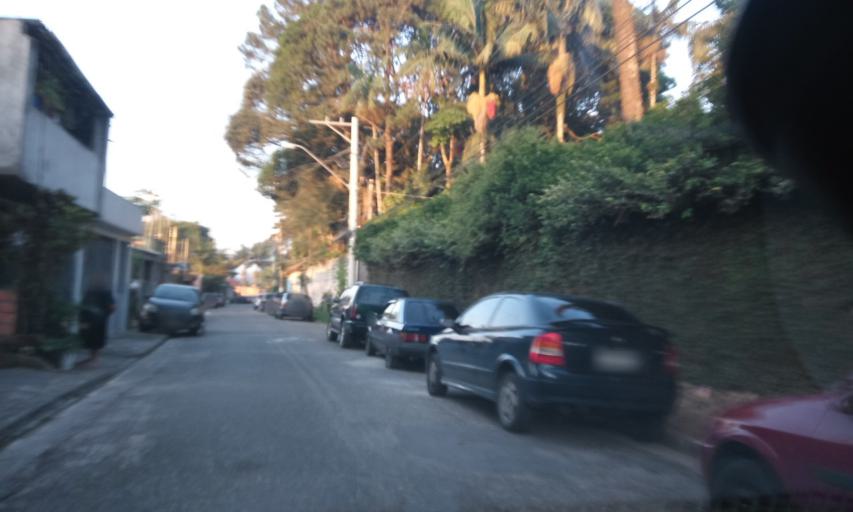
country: BR
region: Sao Paulo
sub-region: Sao Bernardo Do Campo
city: Sao Bernardo do Campo
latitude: -23.7949
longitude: -46.5450
